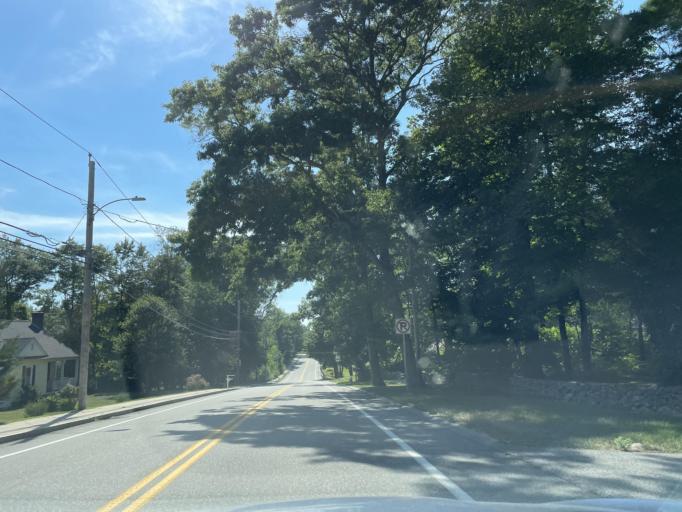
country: US
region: Massachusetts
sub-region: Worcester County
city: Northbridge
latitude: 42.1545
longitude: -71.6763
